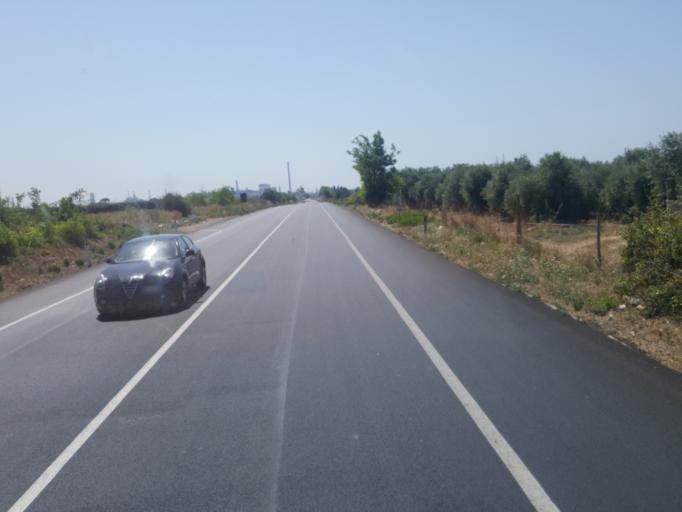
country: IT
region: Apulia
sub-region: Provincia di Taranto
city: Statte
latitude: 40.5253
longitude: 17.1734
